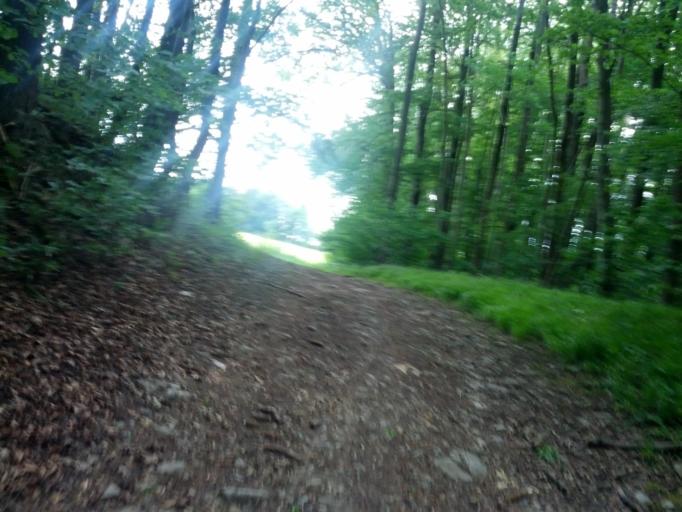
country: DE
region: Thuringia
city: Eisenach
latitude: 50.9454
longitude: 10.3498
